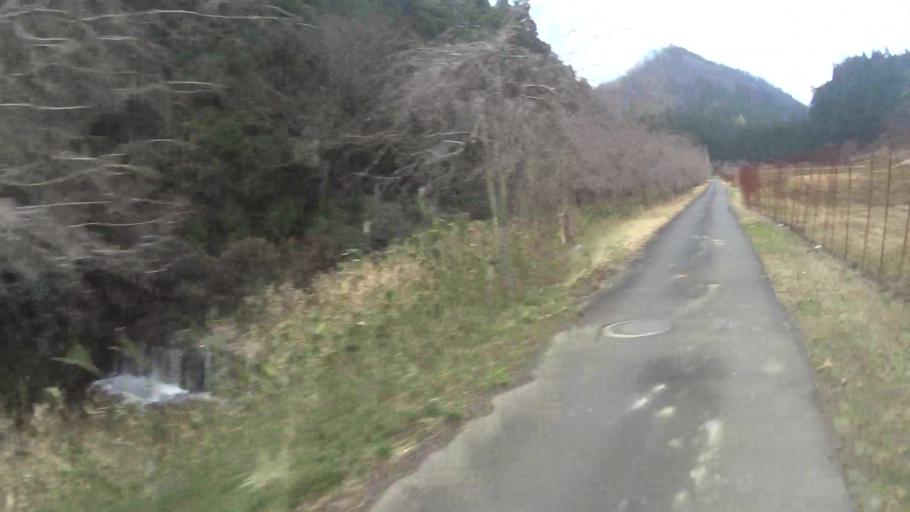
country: JP
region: Kyoto
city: Maizuru
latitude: 35.4439
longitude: 135.4384
